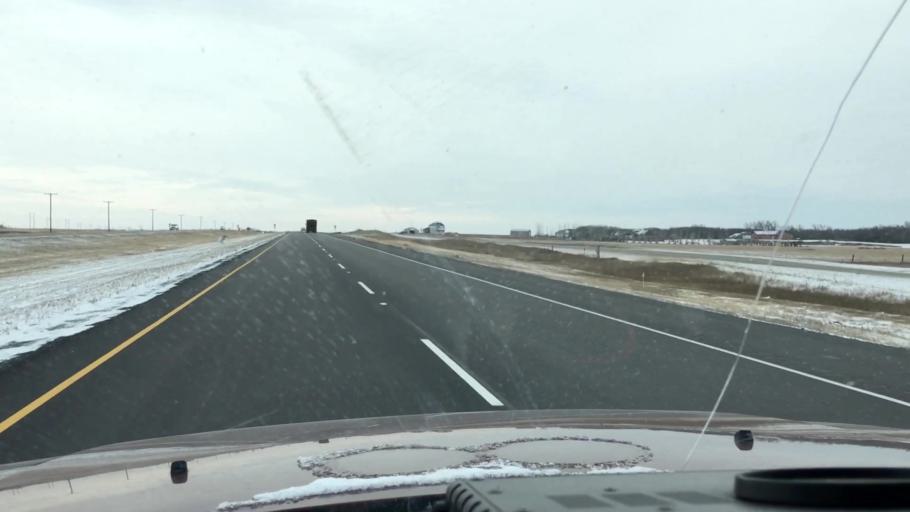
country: CA
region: Saskatchewan
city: Saskatoon
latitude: 51.9334
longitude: -106.5369
